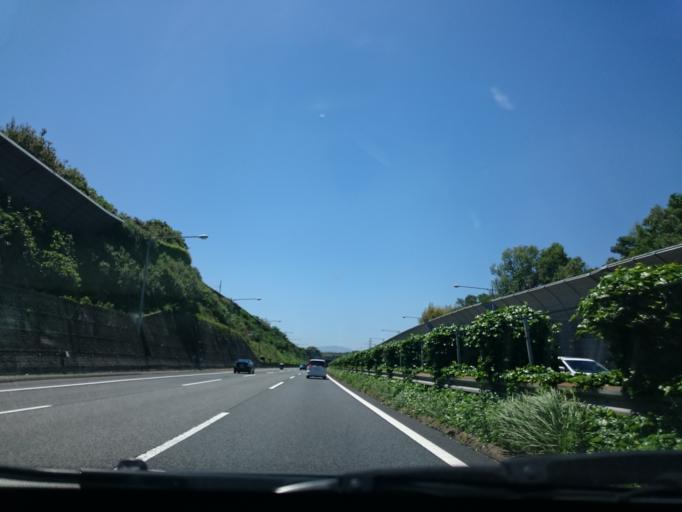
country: JP
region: Kanagawa
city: Isehara
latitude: 35.4177
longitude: 139.3278
